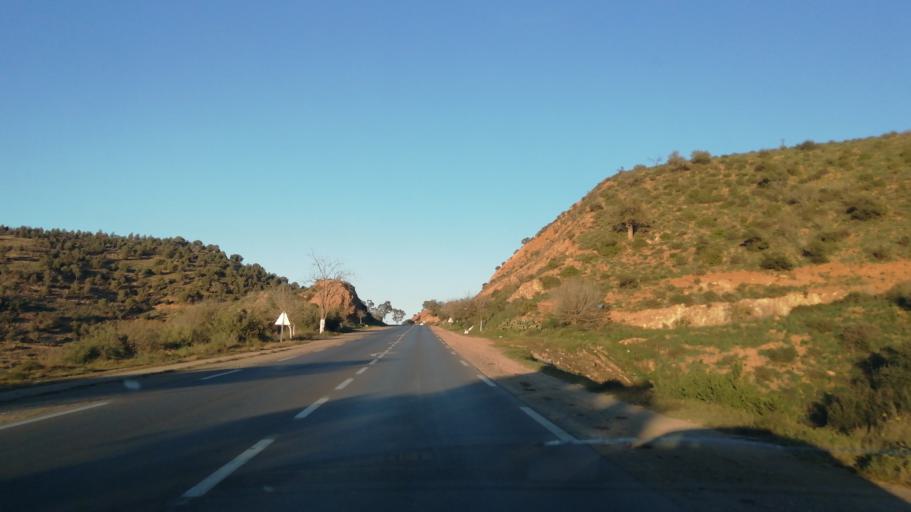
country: DZ
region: Tlemcen
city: Nedroma
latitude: 34.8691
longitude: -1.6711
